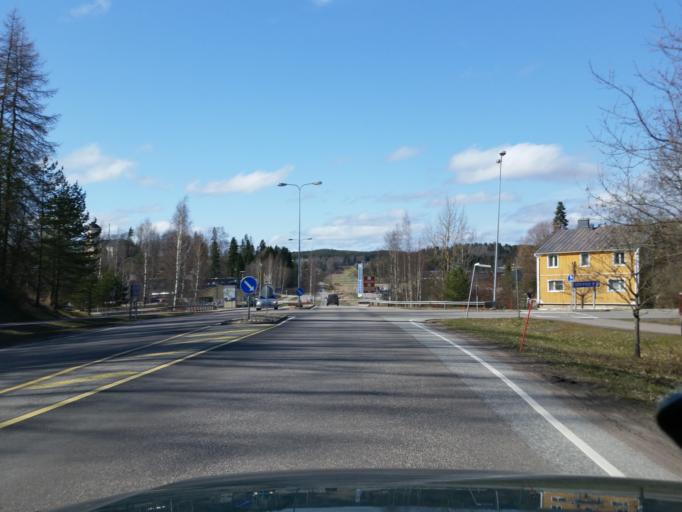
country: FI
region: Uusimaa
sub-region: Helsinki
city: Vihti
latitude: 60.4154
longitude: 24.3277
